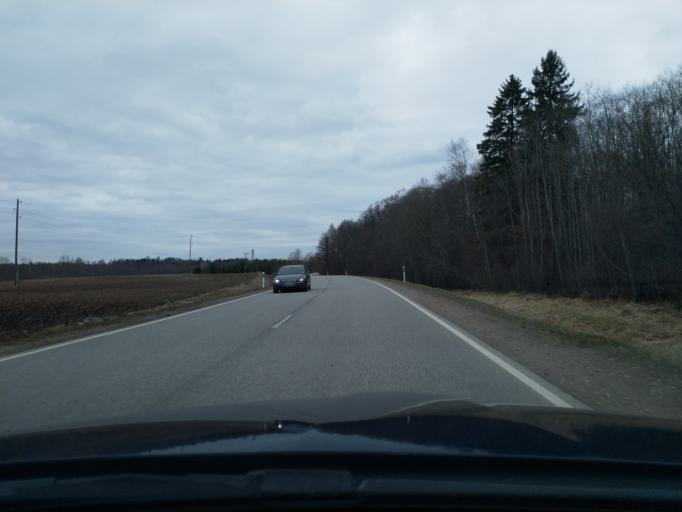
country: LV
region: Kuldigas Rajons
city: Kuldiga
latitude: 56.9617
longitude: 22.0754
